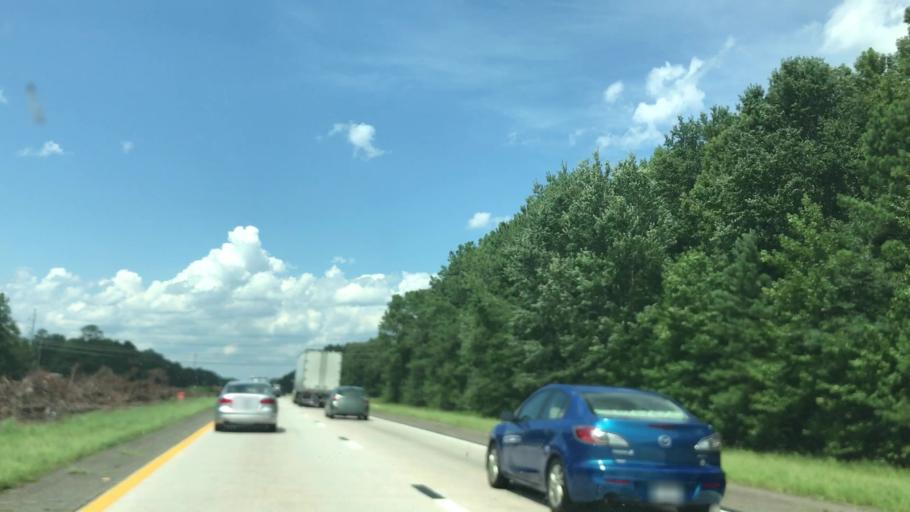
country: US
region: South Carolina
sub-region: Jasper County
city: Hardeeville
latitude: 32.3364
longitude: -81.0493
